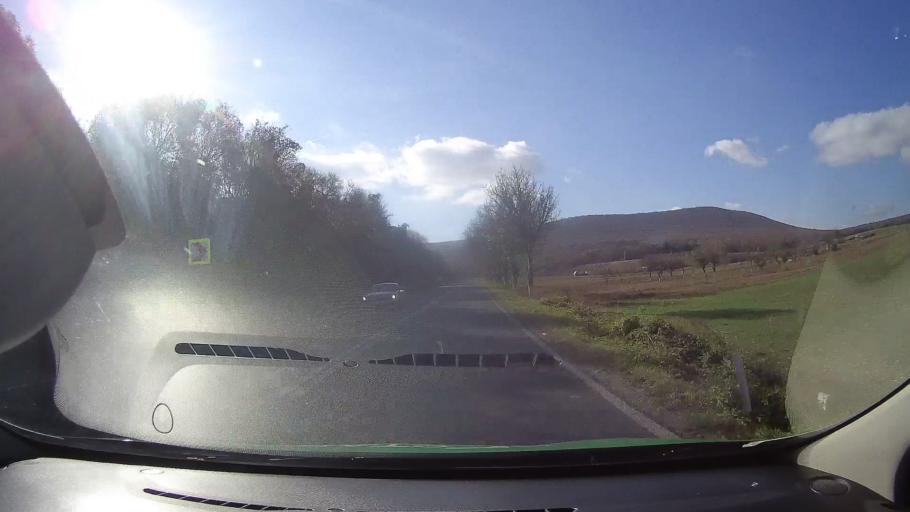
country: RO
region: Tulcea
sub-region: Oras Babadag
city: Babadag
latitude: 44.8767
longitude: 28.6912
